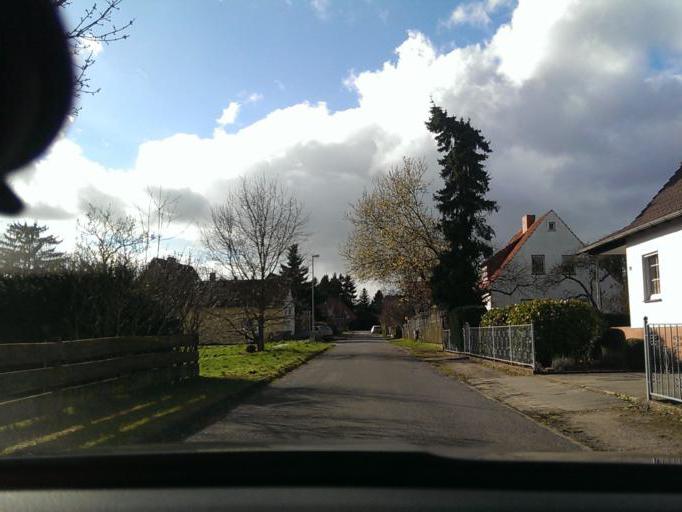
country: DE
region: Lower Saxony
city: Lindwedel
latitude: 52.5561
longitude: 9.6869
